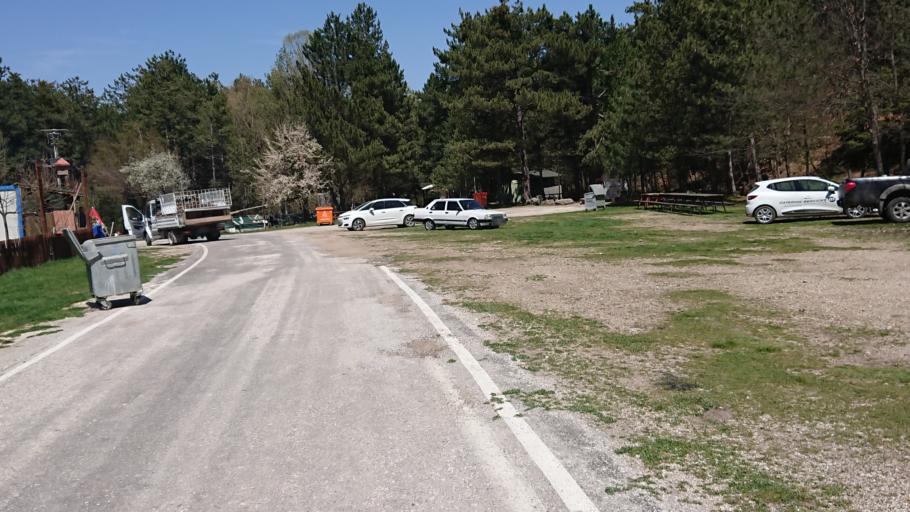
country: TR
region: Kuetahya
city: Sabuncu
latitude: 39.5134
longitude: 30.4242
